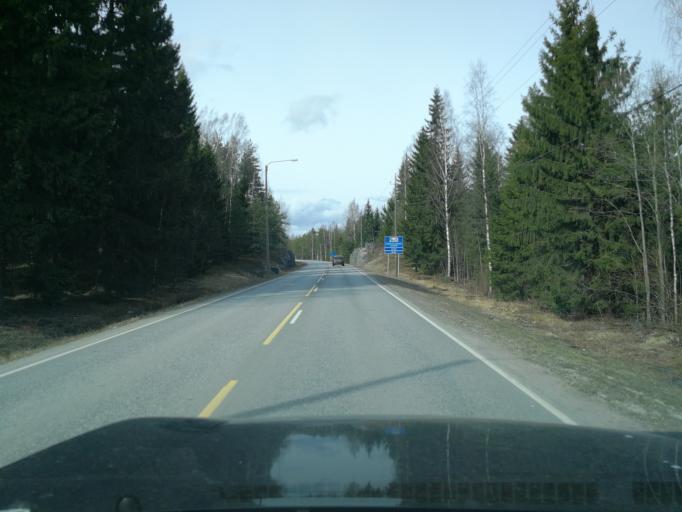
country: FI
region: Uusimaa
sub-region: Helsinki
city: Siuntio
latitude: 60.0974
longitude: 24.2517
